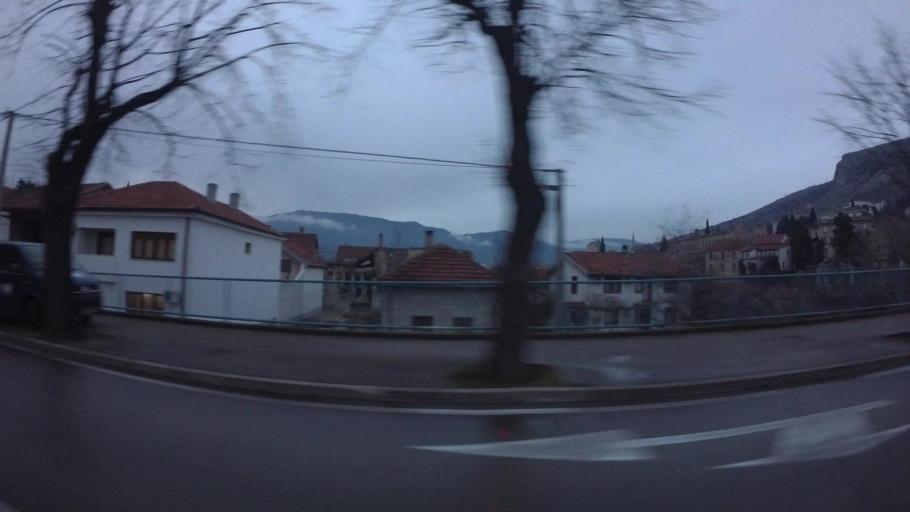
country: BA
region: Federation of Bosnia and Herzegovina
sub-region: Hercegovacko-Bosanski Kanton
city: Mostar
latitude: 43.3352
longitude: 17.8155
